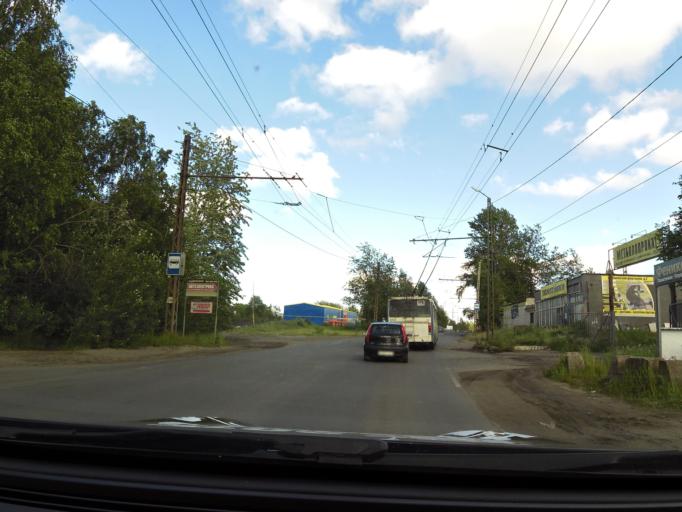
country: RU
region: Republic of Karelia
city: Petrozavodsk
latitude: 61.7730
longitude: 34.4237
